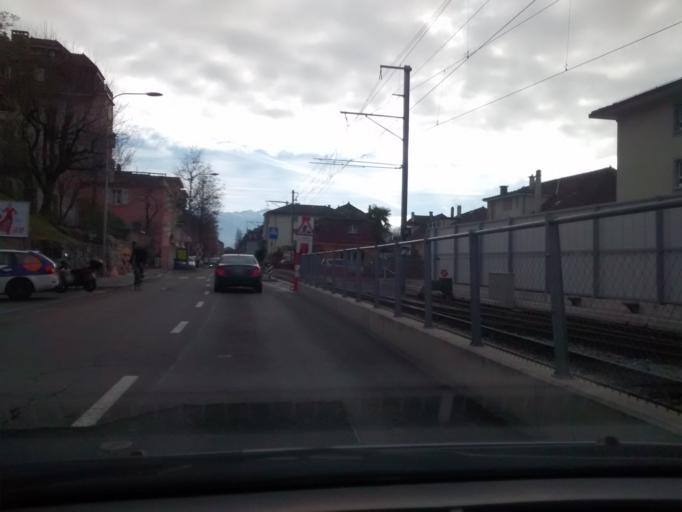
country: CH
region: Vaud
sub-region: Lausanne District
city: Blecherette
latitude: 46.5336
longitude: 6.6108
